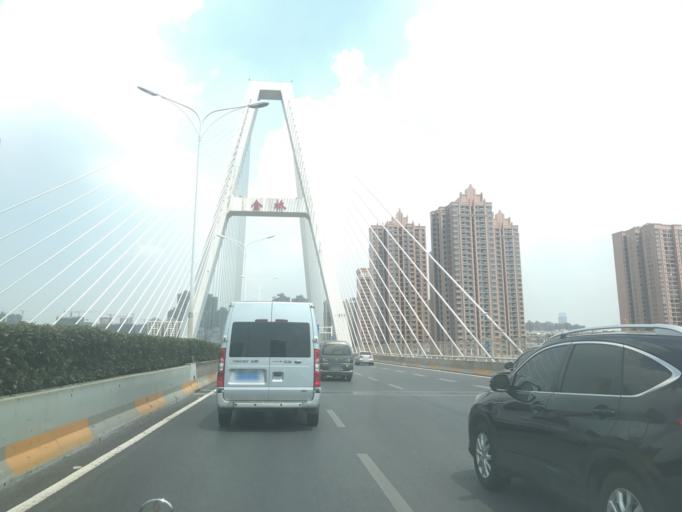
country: CN
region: Hubei
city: Jiang'an
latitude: 30.6288
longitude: 114.2824
